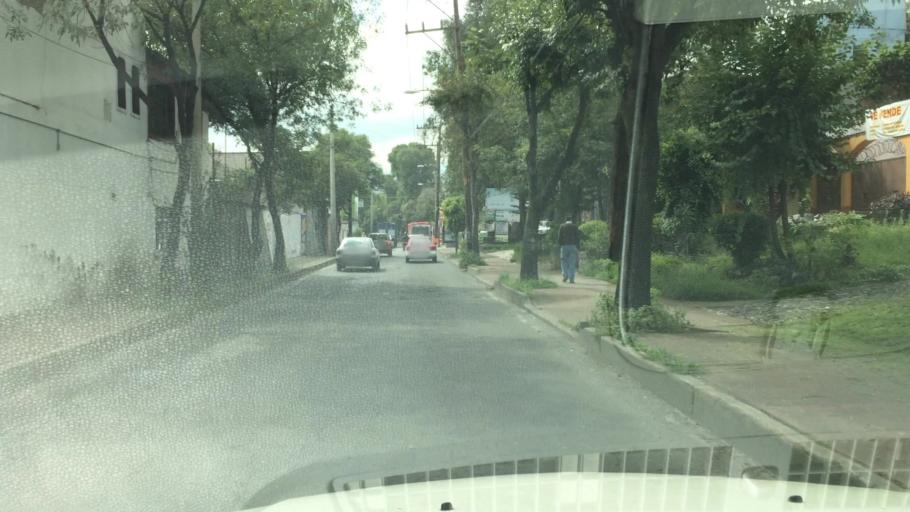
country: MX
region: Mexico City
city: Xochimilco
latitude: 19.2736
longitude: -99.1322
